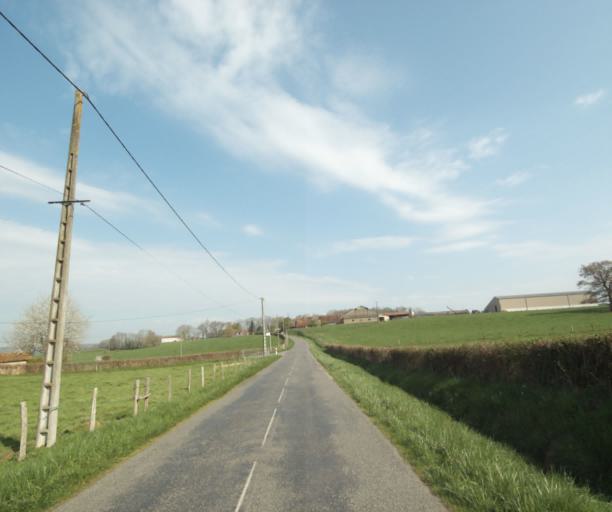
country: FR
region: Bourgogne
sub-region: Departement de Saone-et-Loire
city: Palinges
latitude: 46.5087
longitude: 4.2069
